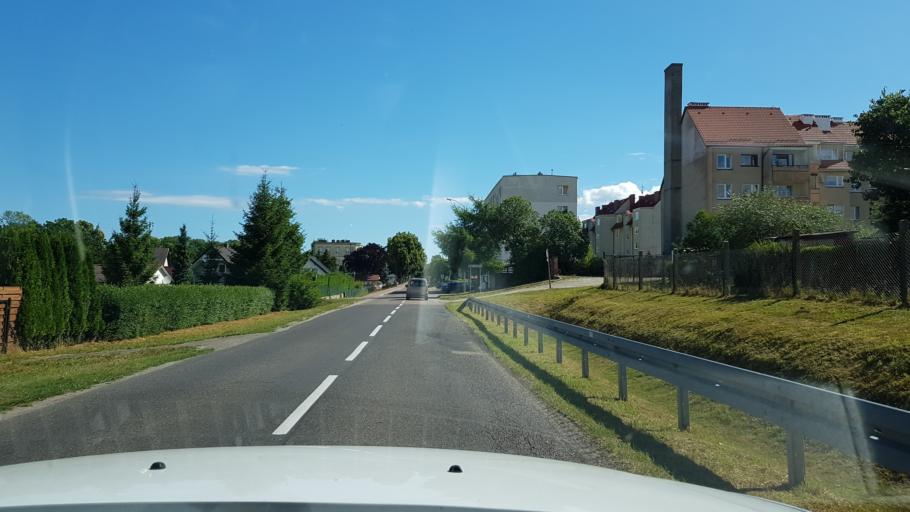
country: PL
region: West Pomeranian Voivodeship
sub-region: Powiat gryficki
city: Trzebiatow
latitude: 54.0535
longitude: 15.2539
